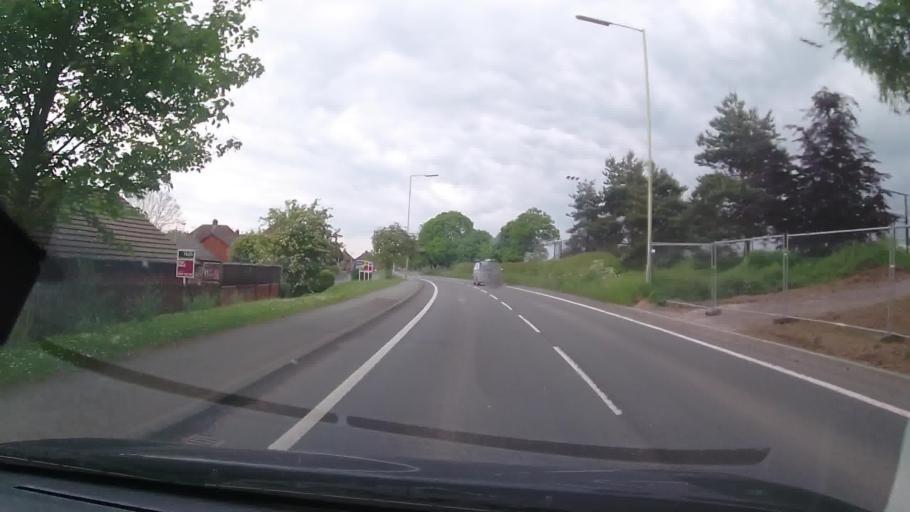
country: GB
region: England
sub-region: Shropshire
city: Ellesmere
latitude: 52.9034
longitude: -2.9059
